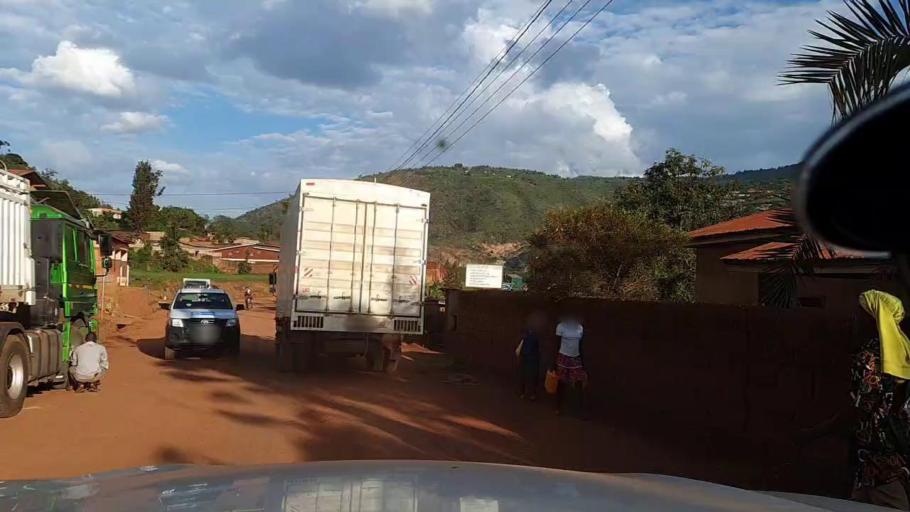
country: RW
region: Kigali
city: Kigali
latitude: -1.9477
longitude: 30.0179
